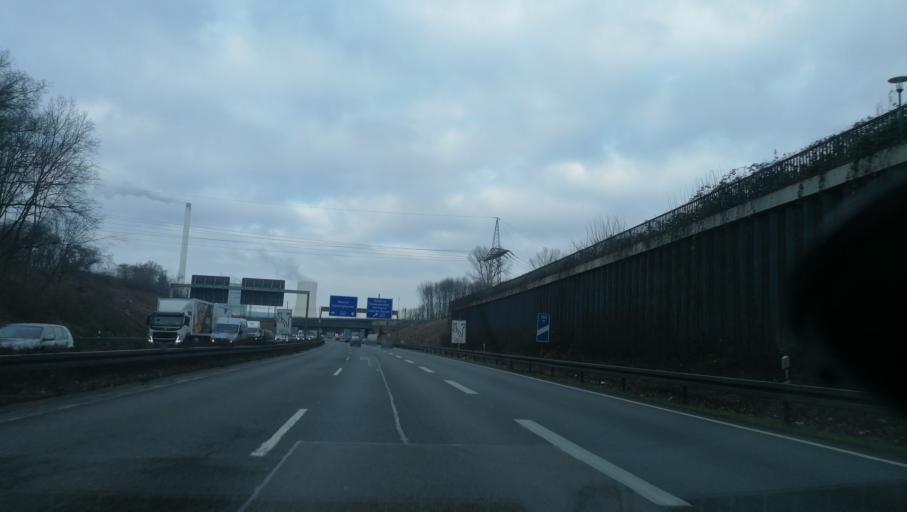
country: DE
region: North Rhine-Westphalia
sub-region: Regierungsbezirk Arnsberg
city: Herne
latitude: 51.5398
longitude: 7.2082
